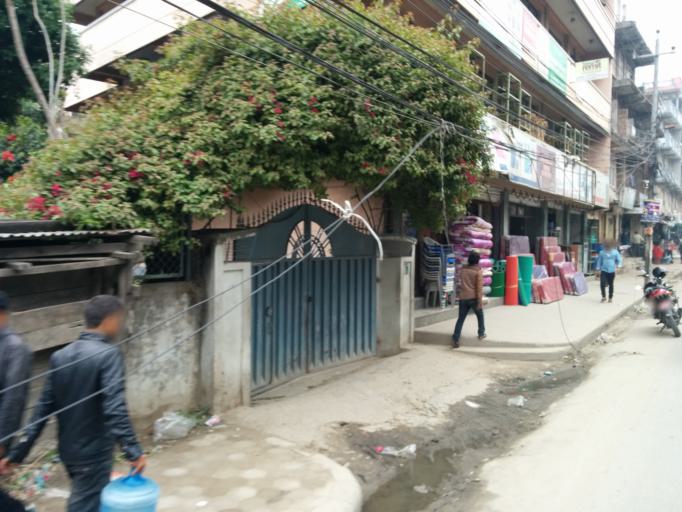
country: NP
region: Central Region
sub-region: Bagmati Zone
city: Kathmandu
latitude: 27.7209
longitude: 85.3665
